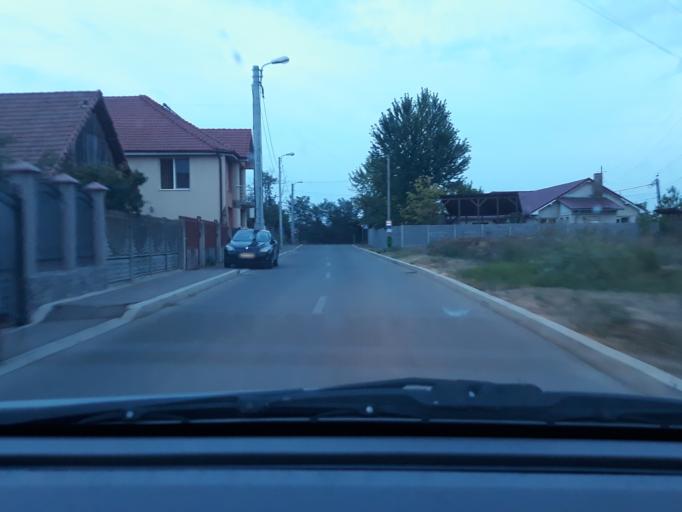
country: RO
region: Bihor
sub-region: Comuna Biharea
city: Oradea
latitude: 47.0348
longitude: 21.9348
